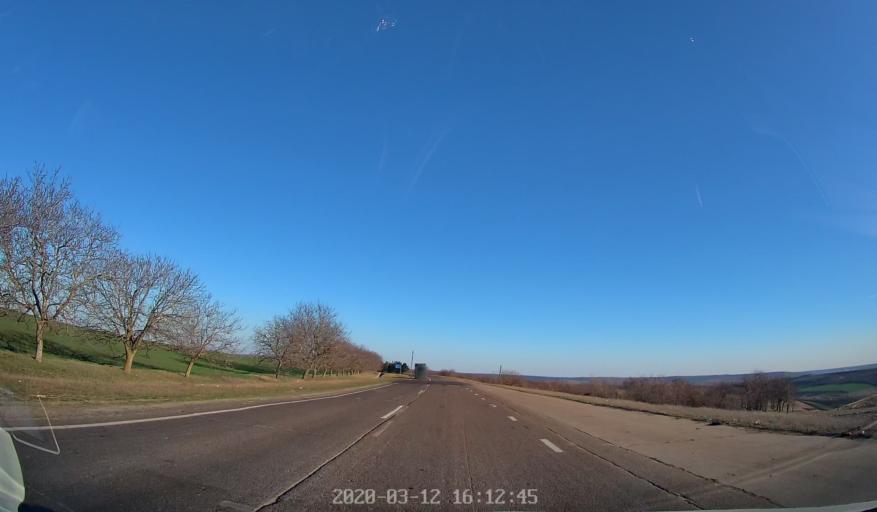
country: MD
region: Anenii Noi
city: Anenii Noi
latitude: 46.9314
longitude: 29.2773
